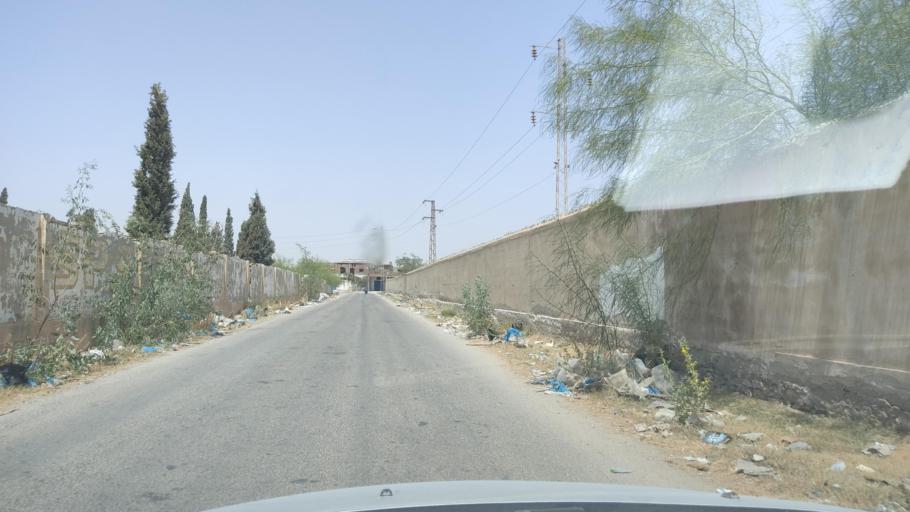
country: TN
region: Safaqis
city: Sfax
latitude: 34.7055
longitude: 10.7154
